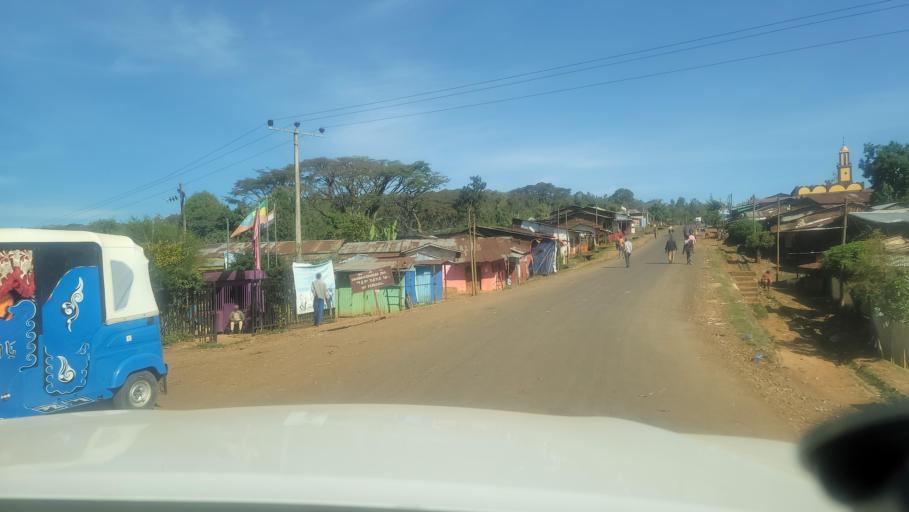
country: ET
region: Oromiya
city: Agaro
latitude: 7.7957
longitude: 36.4774
